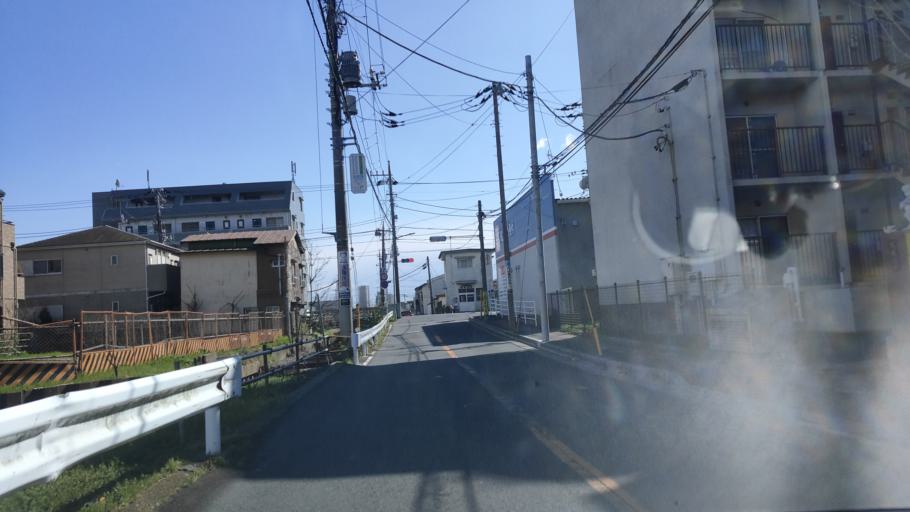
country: JP
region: Chiba
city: Matsudo
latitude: 35.7451
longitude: 139.9243
